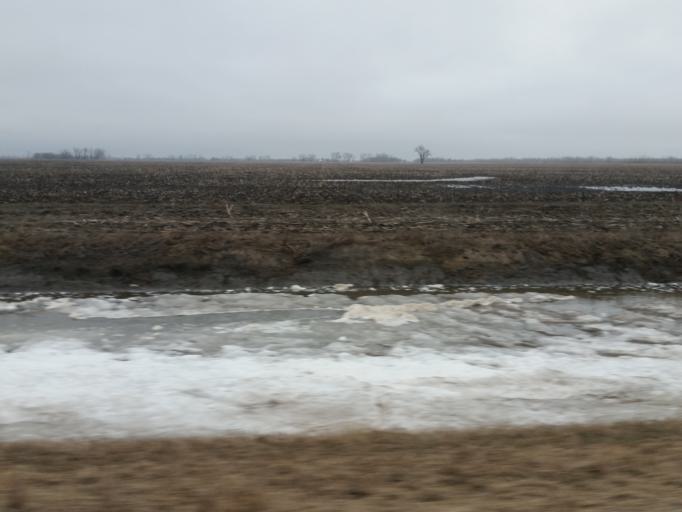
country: US
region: North Dakota
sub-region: Walsh County
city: Grafton
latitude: 48.3687
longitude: -97.1735
